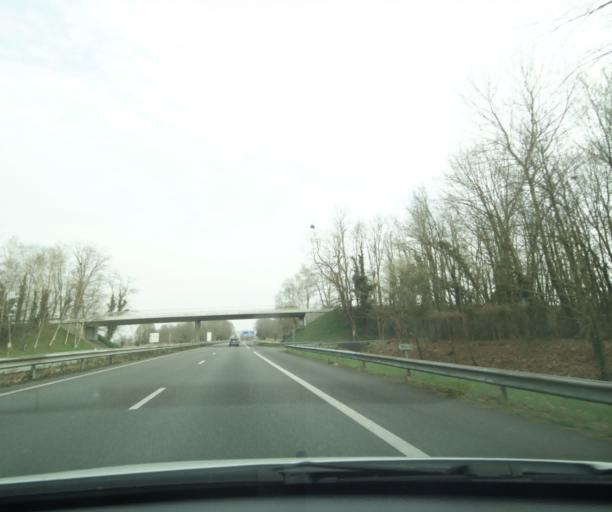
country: FR
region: Aquitaine
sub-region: Departement des Pyrenees-Atlantiques
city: Poey-de-Lescar
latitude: 43.3592
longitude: -0.4622
